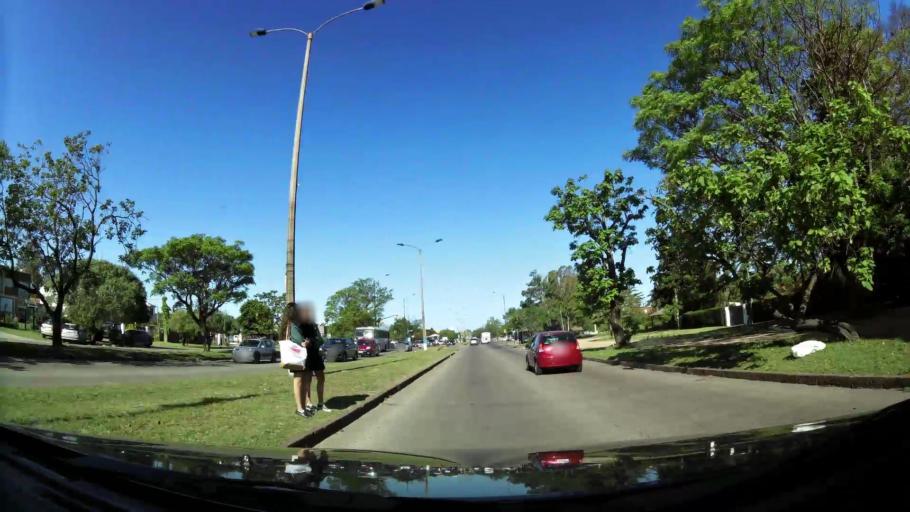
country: UY
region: Canelones
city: Paso de Carrasco
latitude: -34.8783
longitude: -56.0689
